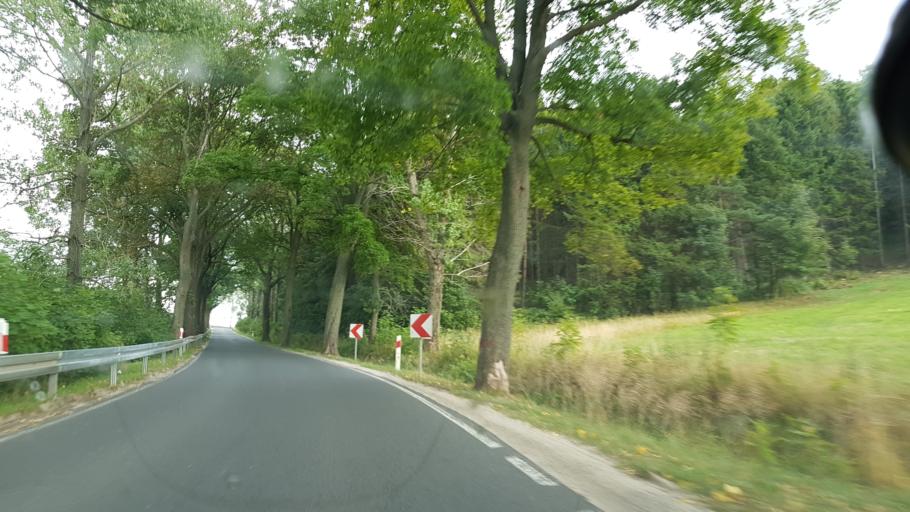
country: PL
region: Lower Silesian Voivodeship
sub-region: Powiat jeleniogorski
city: Janowice Wielkie
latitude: 50.8986
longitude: 15.9752
